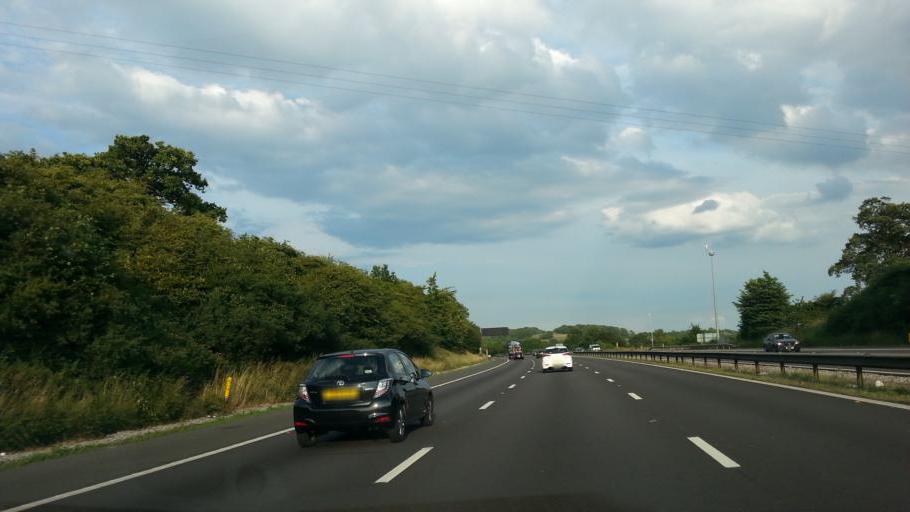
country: GB
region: England
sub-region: Worcestershire
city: Alvechurch
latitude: 52.3558
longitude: -1.9242
